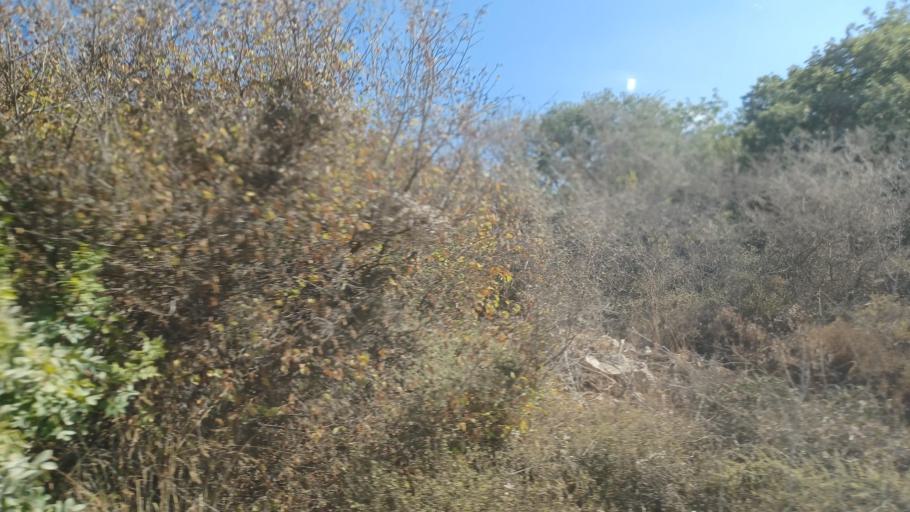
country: CY
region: Pafos
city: Polis
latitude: 34.9834
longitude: 32.4941
